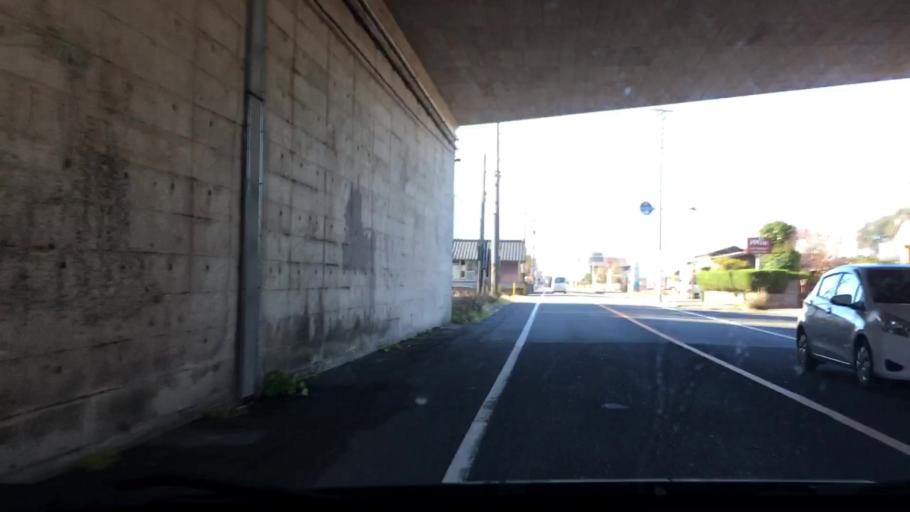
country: JP
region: Kagoshima
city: Kajiki
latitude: 31.7933
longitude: 130.7166
